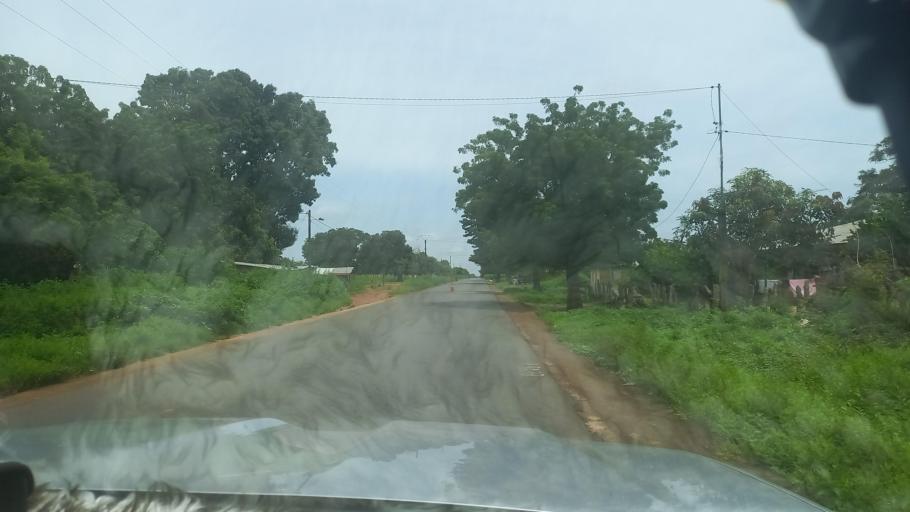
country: SN
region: Kolda
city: Marsassoum
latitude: 12.9619
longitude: -15.9854
